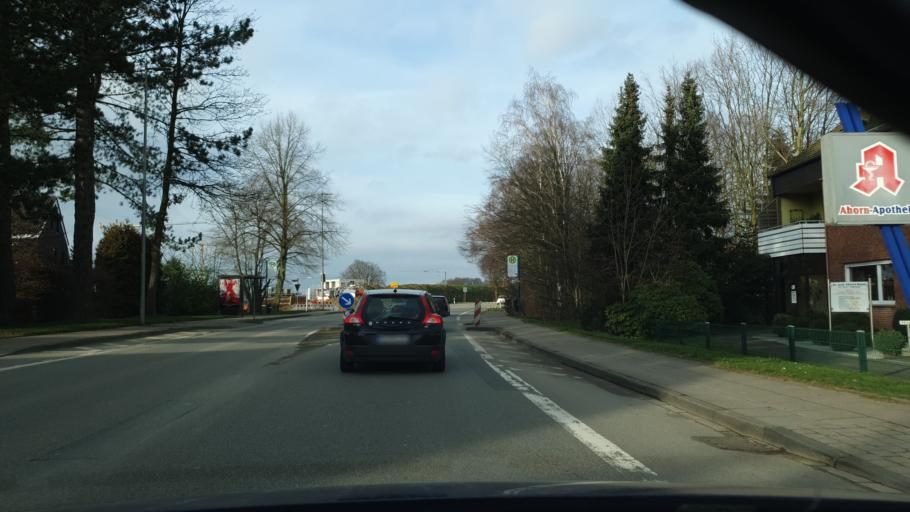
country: DE
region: North Rhine-Westphalia
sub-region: Regierungsbezirk Detmold
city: Bielefeld
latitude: 52.0734
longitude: 8.5148
